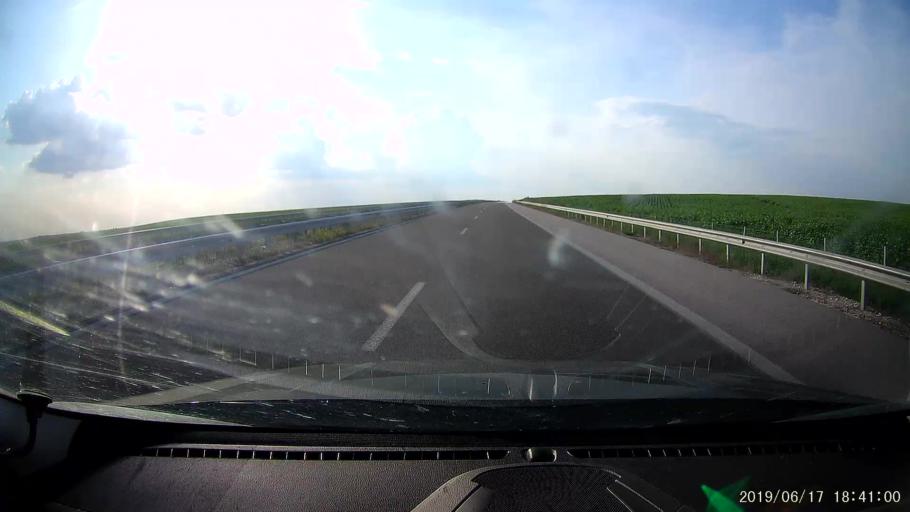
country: BG
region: Stara Zagora
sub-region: Obshtina Chirpan
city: Chirpan
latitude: 42.1641
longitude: 25.2643
